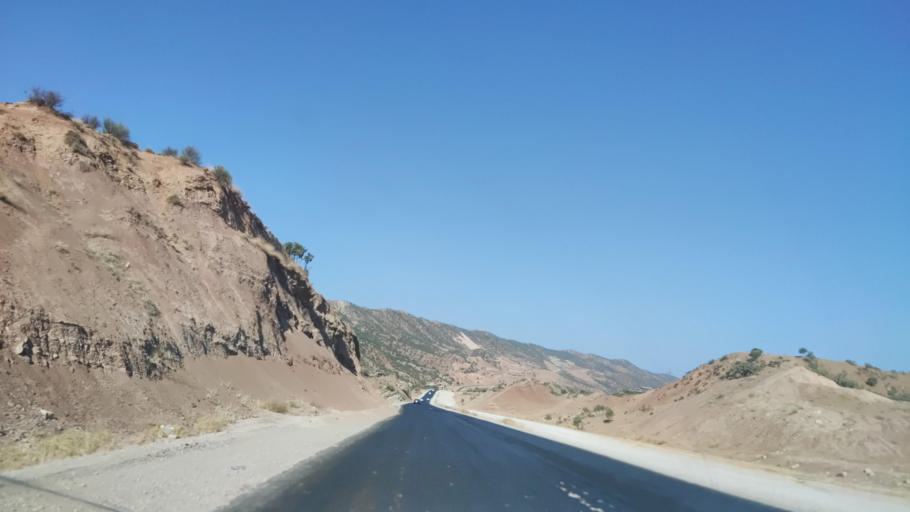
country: IQ
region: Arbil
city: Shaqlawah
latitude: 36.4298
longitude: 44.3339
